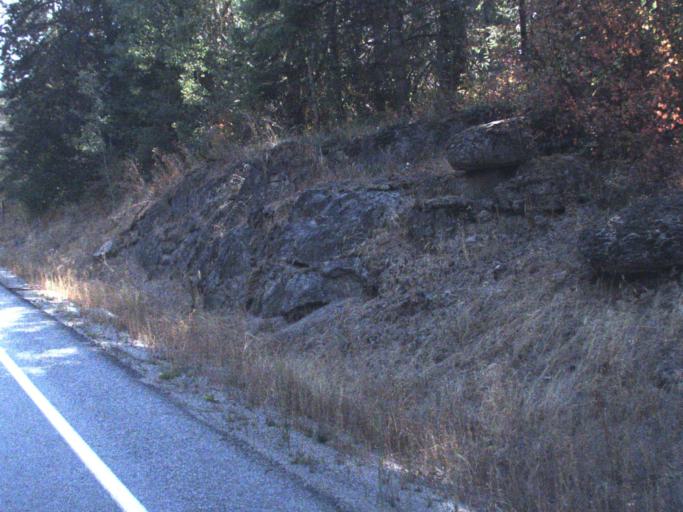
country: US
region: Washington
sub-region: Pend Oreille County
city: Newport
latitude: 48.1130
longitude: -117.2757
